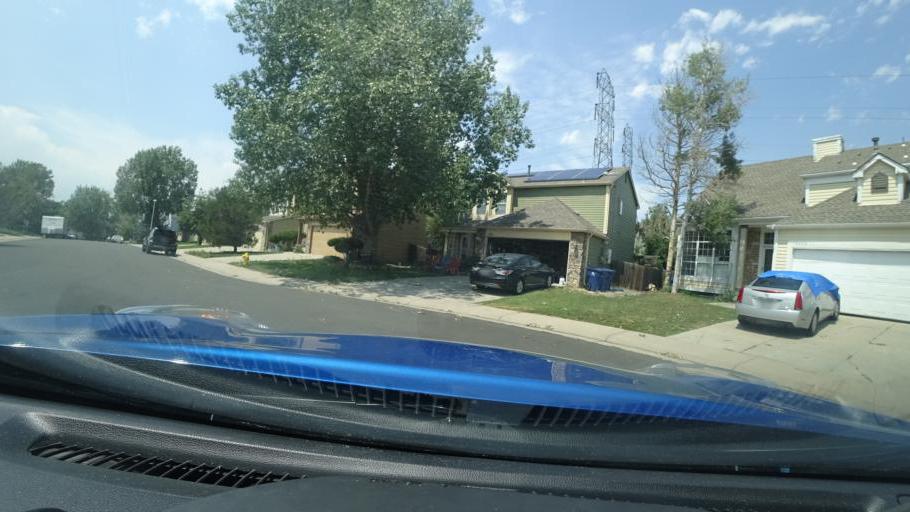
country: US
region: Colorado
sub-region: Adams County
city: Aurora
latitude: 39.6672
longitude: -104.7624
